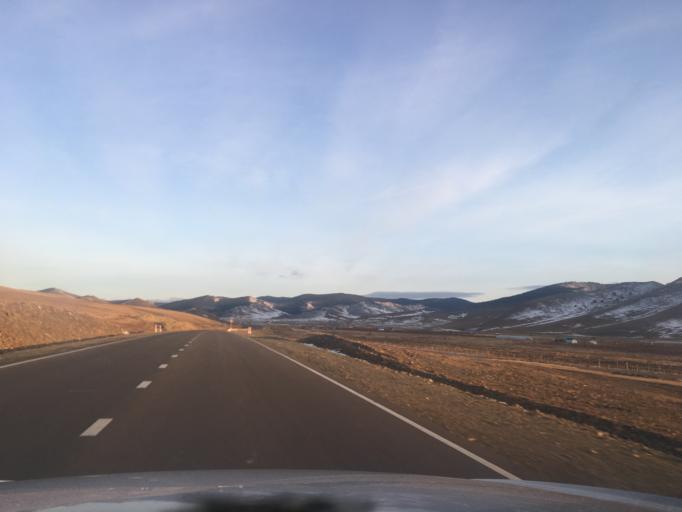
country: MN
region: Central Aimak
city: Mandal
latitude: 48.1113
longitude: 106.7090
